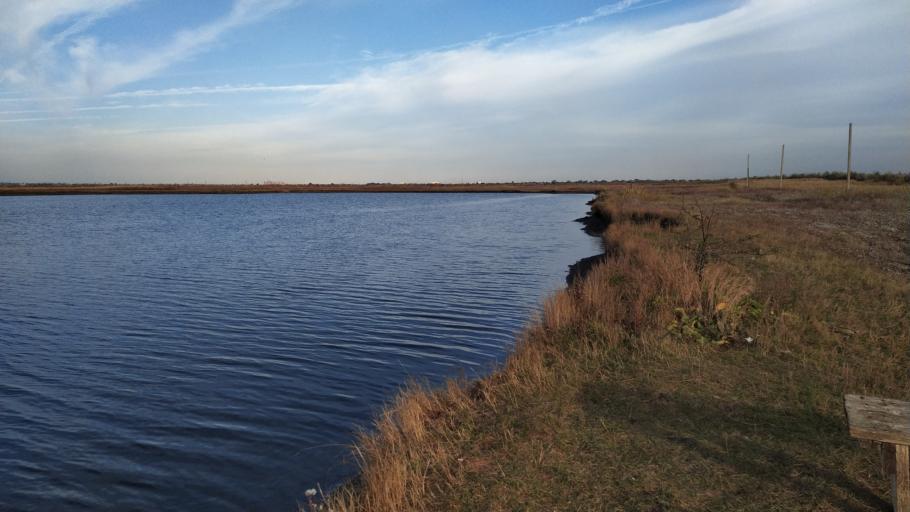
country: RU
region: Rostov
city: Kuleshovka
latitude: 47.1211
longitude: 39.6355
